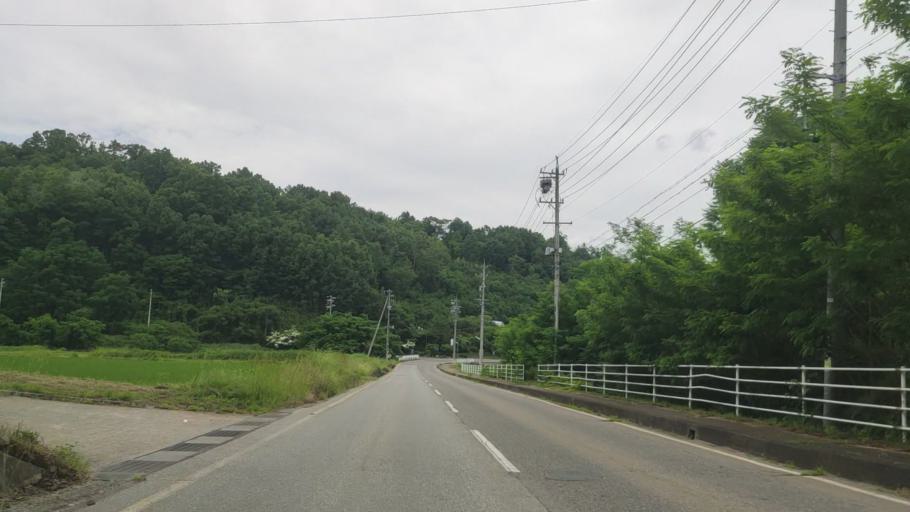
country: JP
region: Nagano
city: Kamimaruko
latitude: 36.3052
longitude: 138.3245
